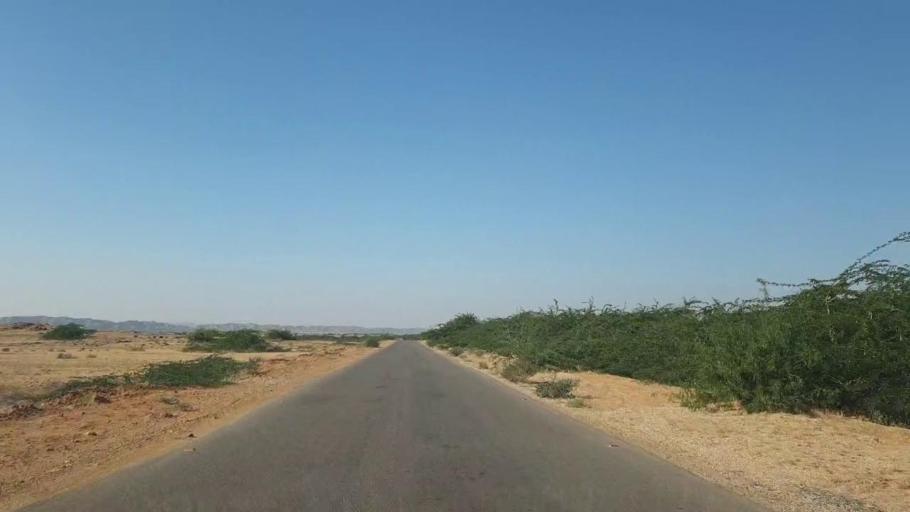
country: PK
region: Sindh
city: Malir Cantonment
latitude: 25.2723
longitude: 67.5916
